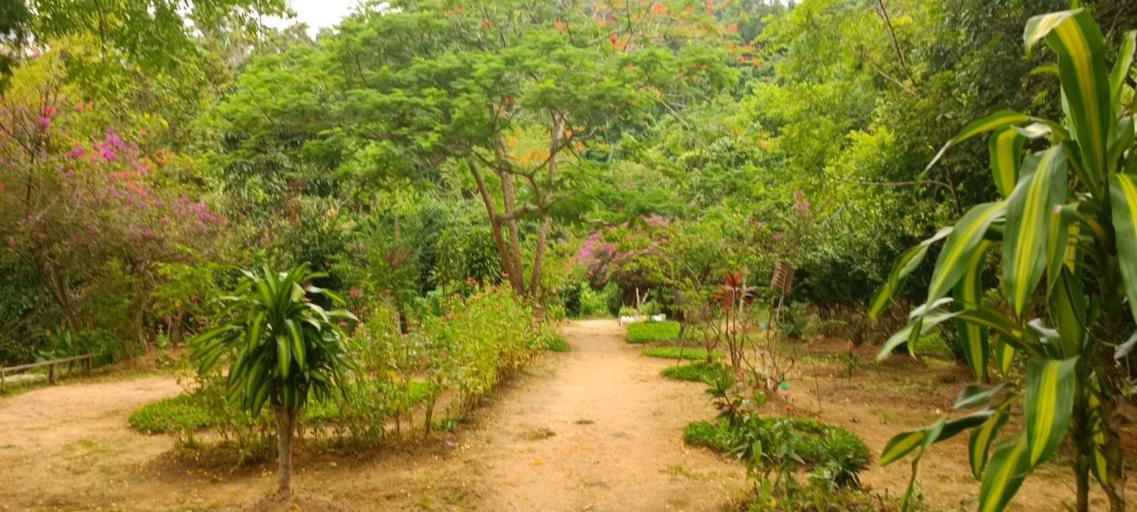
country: MY
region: Penang
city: Tanjung Tokong
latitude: 5.4257
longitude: 100.2936
